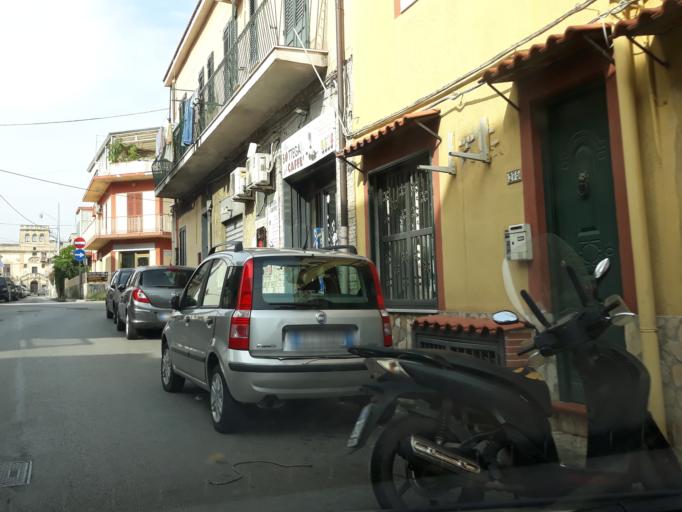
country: IT
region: Sicily
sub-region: Palermo
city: Villa Ciambra
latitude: 38.0861
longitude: 13.3482
